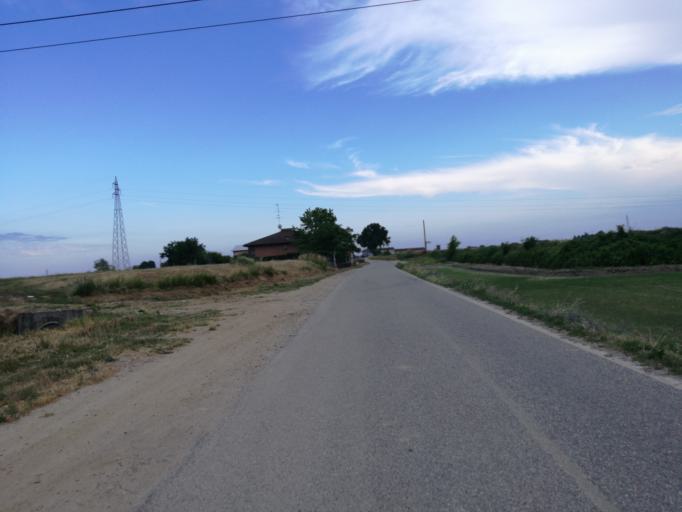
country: IT
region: Piedmont
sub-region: Provincia di Novara
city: Torrion Quartara
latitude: 45.4140
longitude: 8.6191
